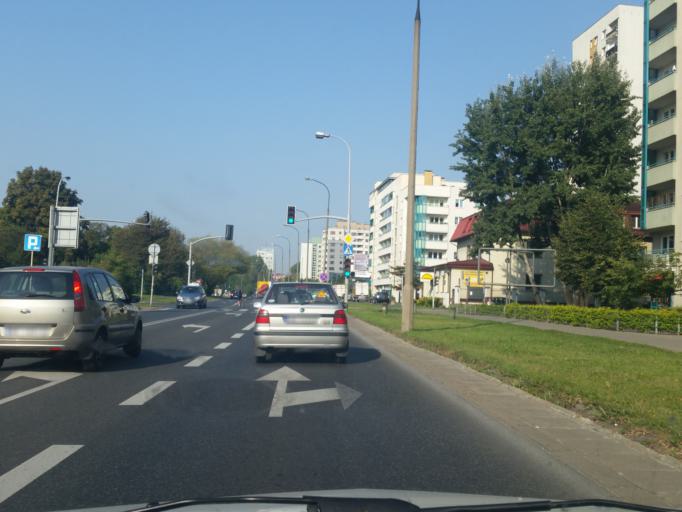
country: PL
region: Masovian Voivodeship
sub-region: Warszawa
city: Mokotow
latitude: 52.1801
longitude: 21.0186
